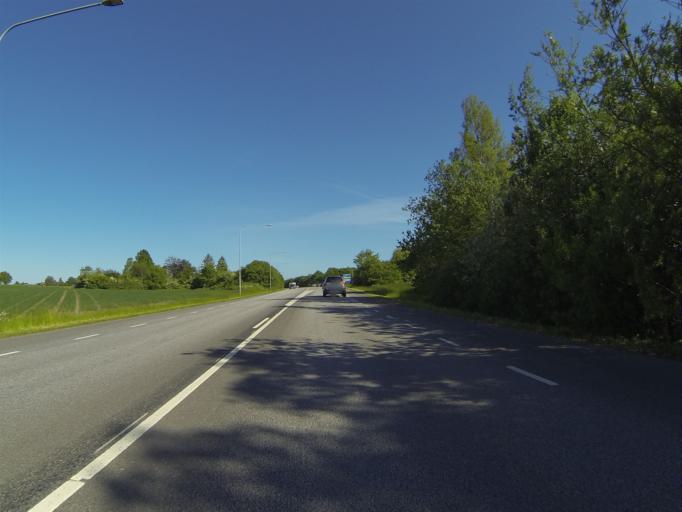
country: SE
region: Skane
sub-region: Burlovs Kommun
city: Arloev
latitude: 55.5928
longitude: 13.1035
